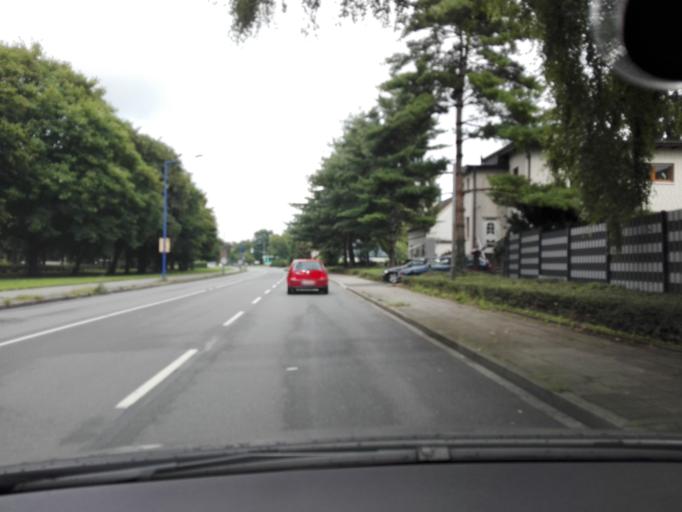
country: DE
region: North Rhine-Westphalia
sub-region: Regierungsbezirk Arnsberg
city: Unna
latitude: 51.5442
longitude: 7.6936
